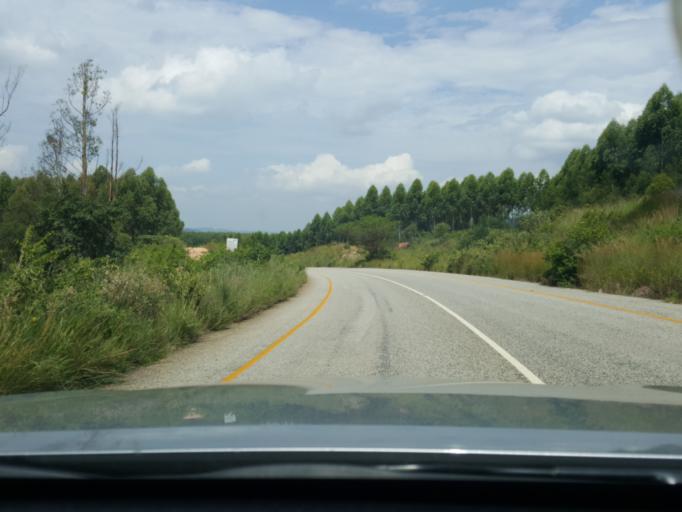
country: ZA
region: Mpumalanga
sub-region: Ehlanzeni District
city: White River
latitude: -25.1866
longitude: 30.8965
